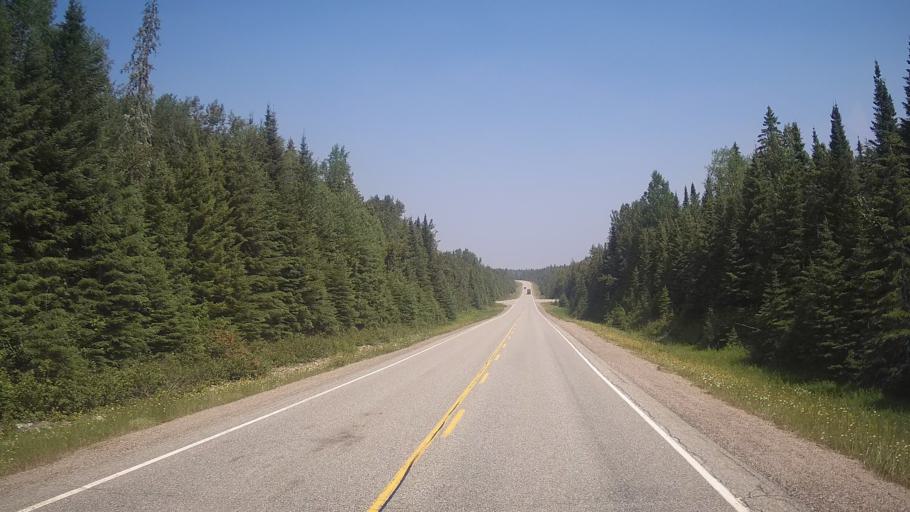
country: CA
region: Ontario
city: Timmins
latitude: 48.0904
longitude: -81.5944
